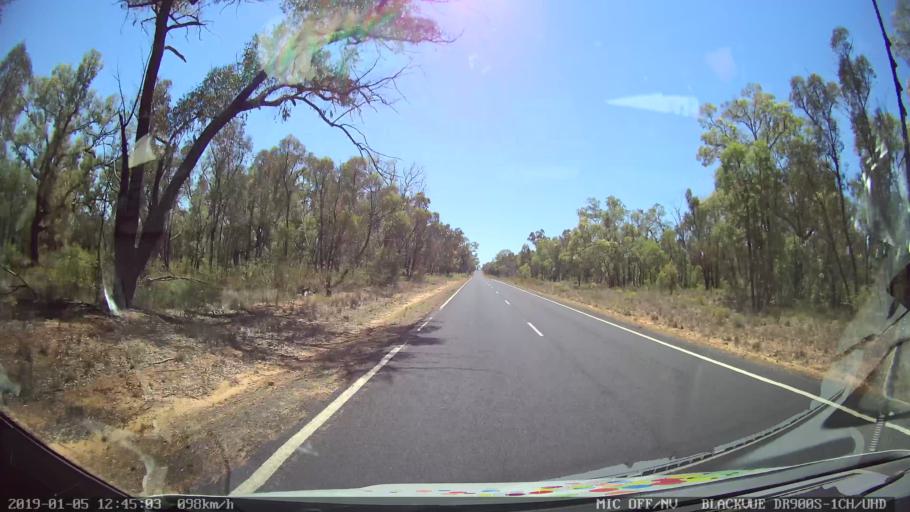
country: AU
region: New South Wales
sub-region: Warrumbungle Shire
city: Coonabarabran
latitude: -31.1316
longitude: 149.5452
